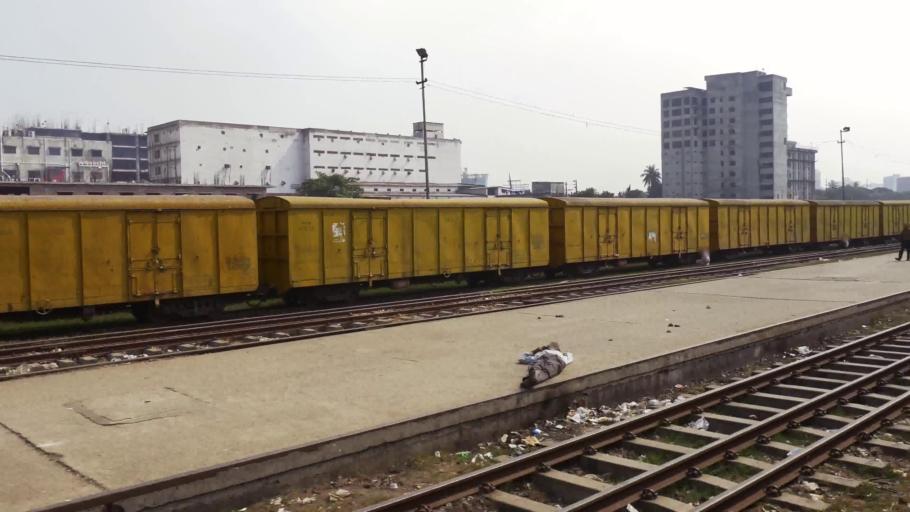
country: BD
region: Dhaka
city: Paltan
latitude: 23.7886
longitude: 90.3995
